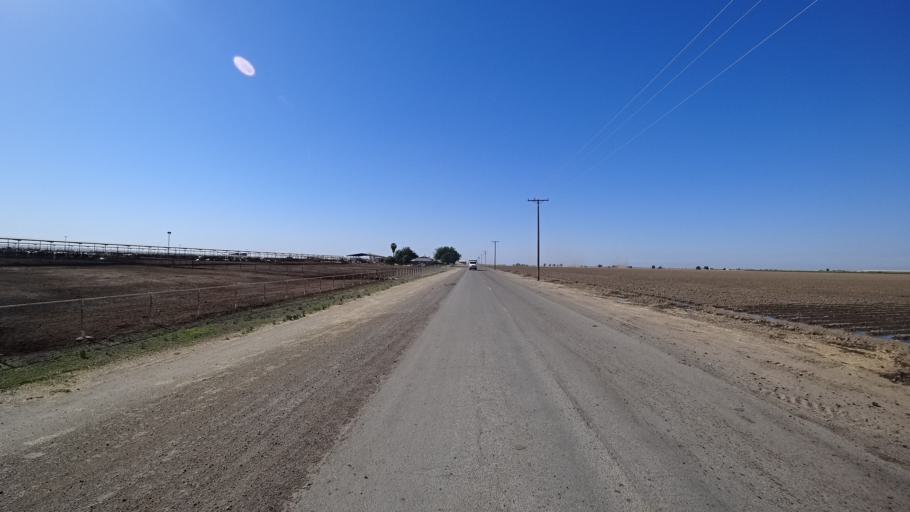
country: US
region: California
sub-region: Kings County
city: Home Garden
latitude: 36.2473
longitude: -119.5562
